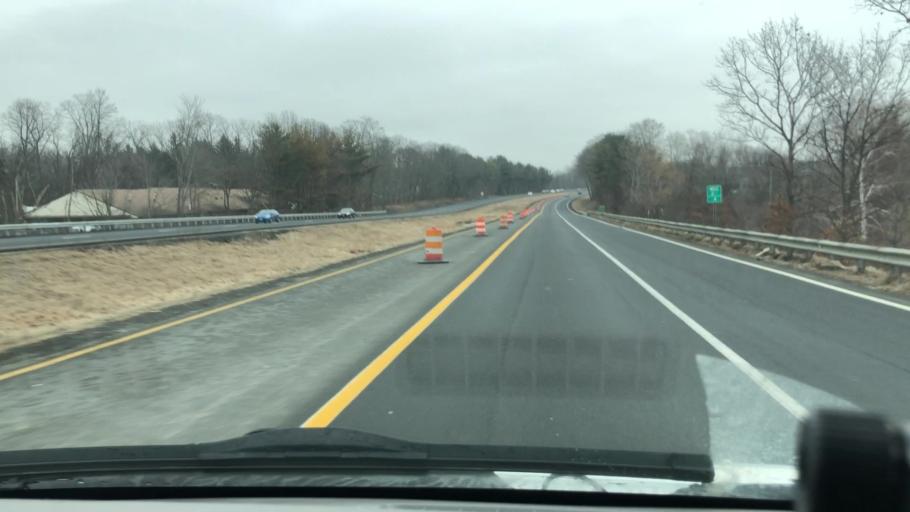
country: US
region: Massachusetts
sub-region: Hampshire County
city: Northampton
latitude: 42.3380
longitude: -72.6321
